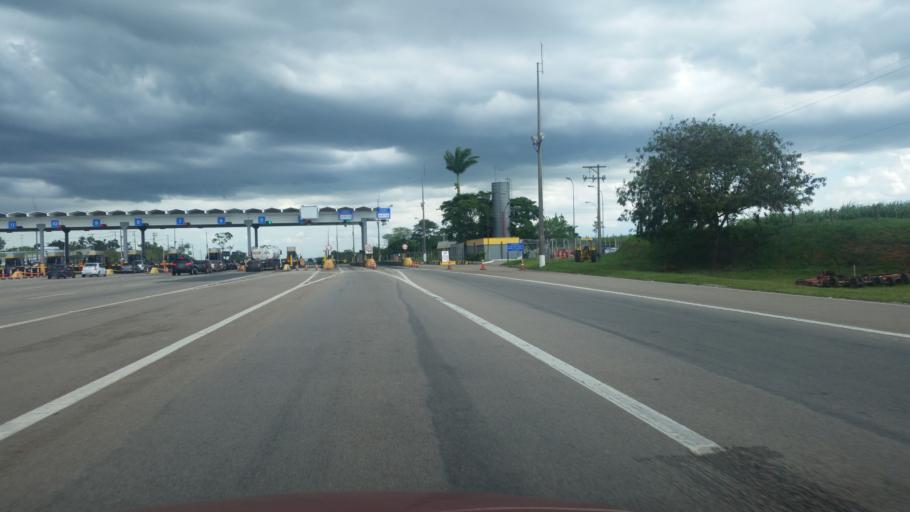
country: BR
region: Sao Paulo
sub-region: Boituva
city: Boituva
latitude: -23.3133
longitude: -47.6448
